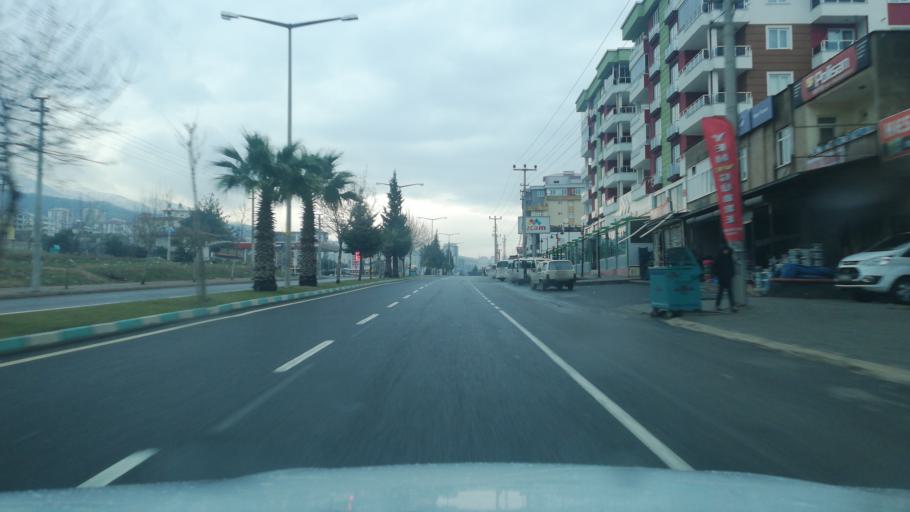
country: TR
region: Kahramanmaras
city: Kahramanmaras
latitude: 37.5817
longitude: 36.9712
